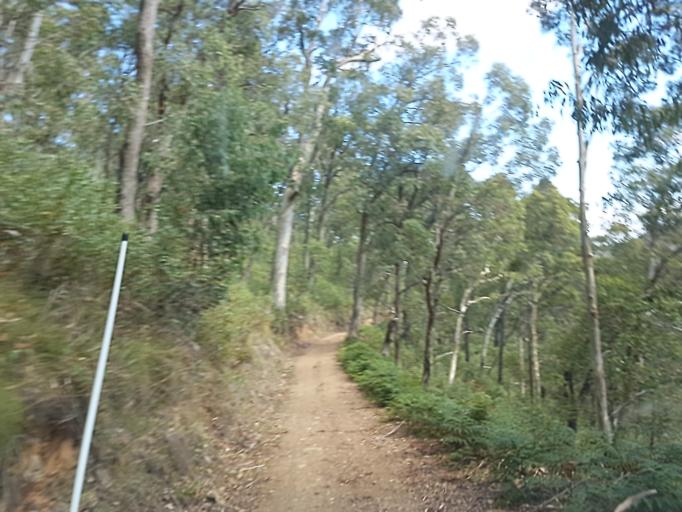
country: AU
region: Victoria
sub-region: Alpine
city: Mount Beauty
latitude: -36.9137
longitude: 147.0003
